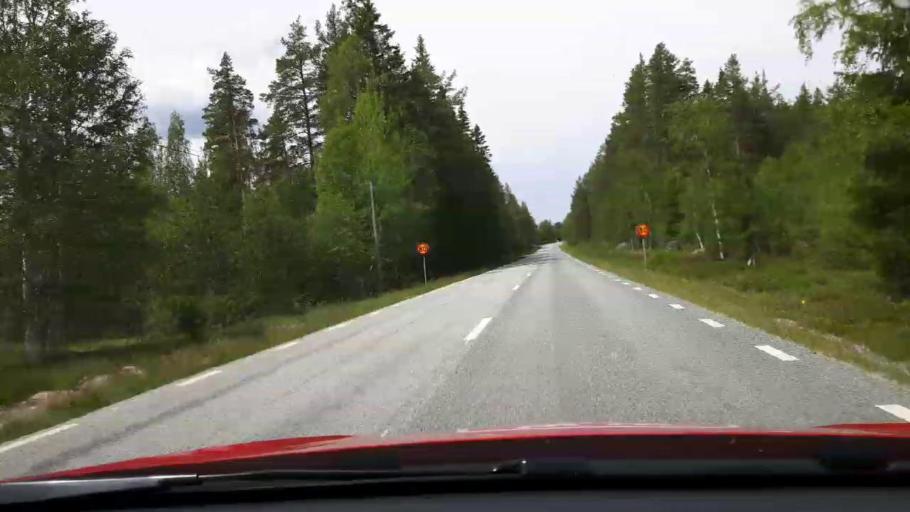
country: SE
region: Jaemtland
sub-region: Harjedalens Kommun
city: Sveg
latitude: 62.1513
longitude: 13.9014
